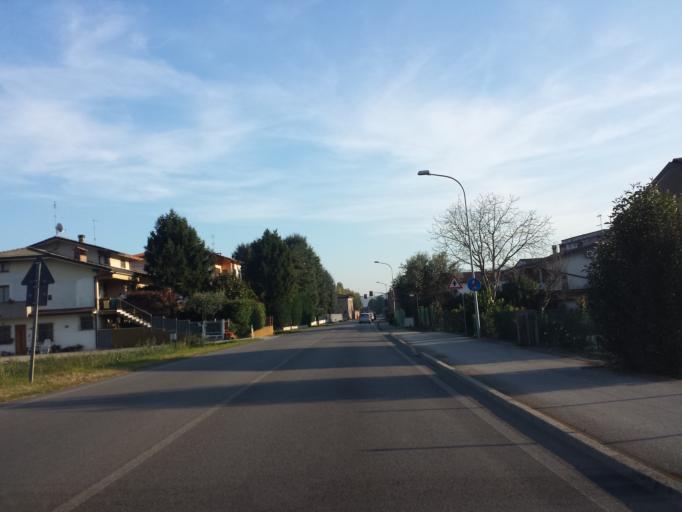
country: IT
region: Veneto
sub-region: Provincia di Vicenza
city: Malo
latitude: 45.6554
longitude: 11.4171
